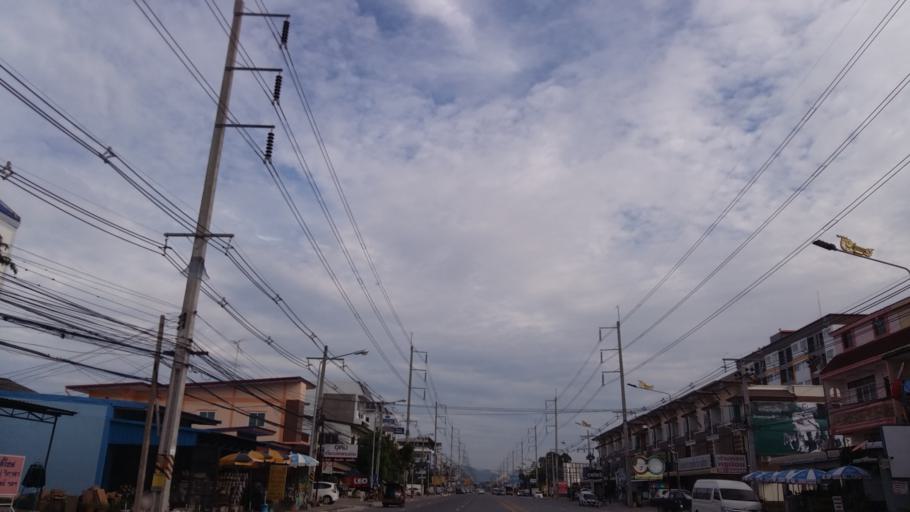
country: TH
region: Chon Buri
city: Chon Buri
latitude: 13.3274
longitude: 100.9400
